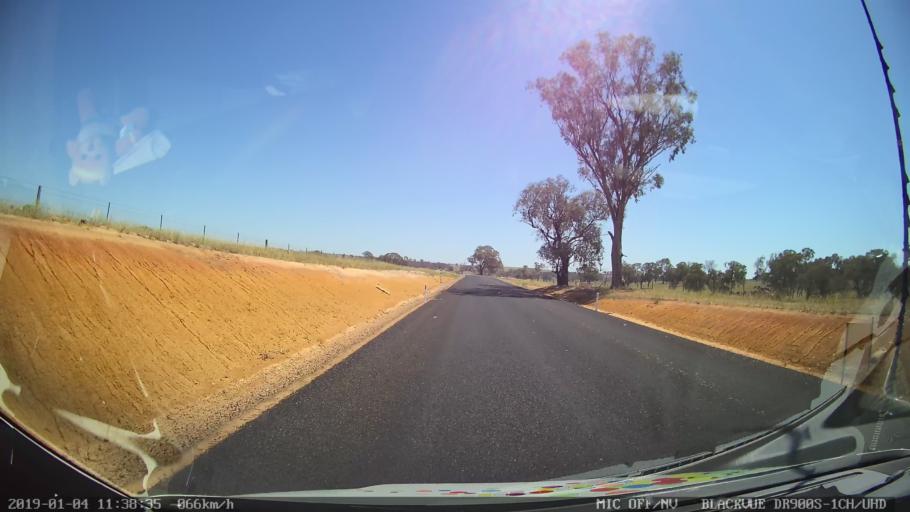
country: AU
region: New South Wales
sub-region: Cabonne
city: Molong
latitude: -33.0214
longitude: 148.8016
